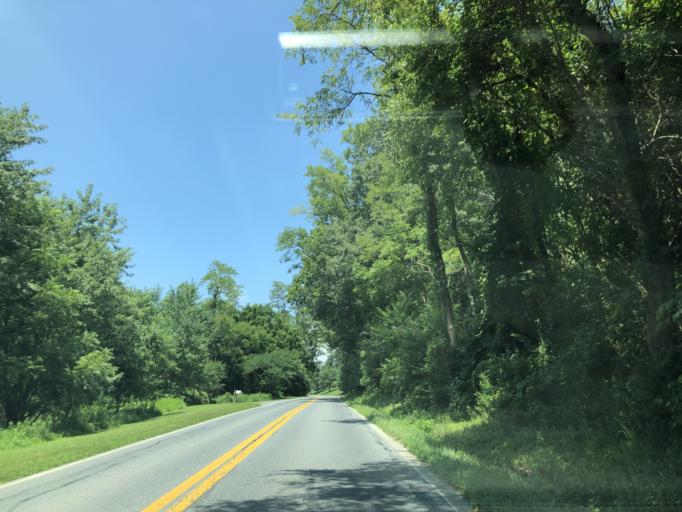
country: US
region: Maryland
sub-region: Carroll County
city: Westminster
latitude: 39.5254
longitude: -76.9529
